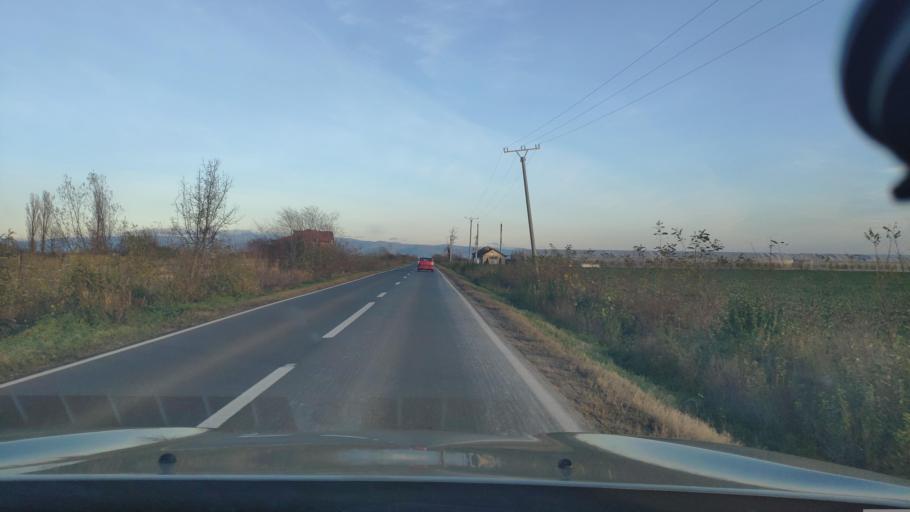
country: RO
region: Satu Mare
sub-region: Comuna Mediesu Aurit
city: Potau
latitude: 47.7729
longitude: 23.1254
